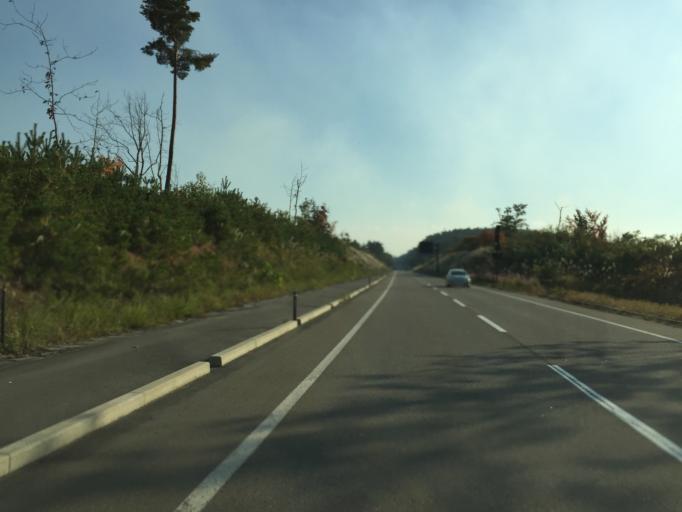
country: JP
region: Fukushima
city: Kitakata
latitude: 37.7201
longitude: 139.8699
